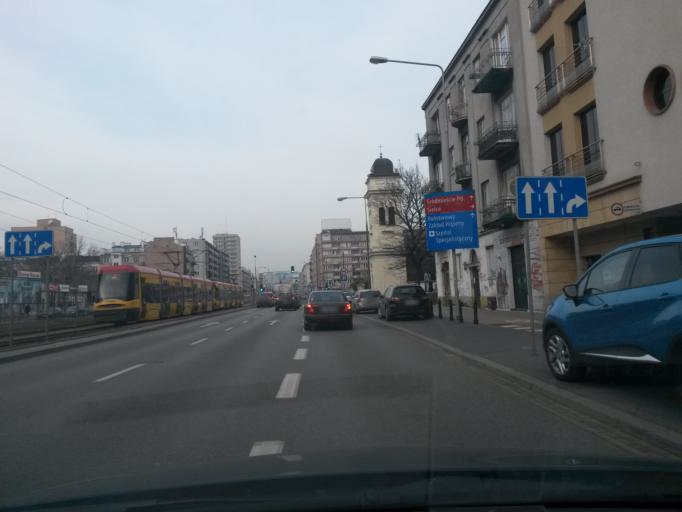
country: PL
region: Masovian Voivodeship
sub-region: Warszawa
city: Mokotow
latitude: 52.1983
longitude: 21.0242
